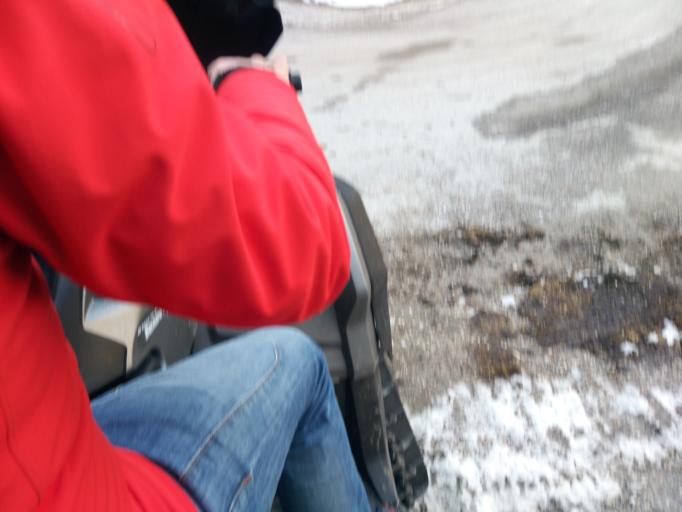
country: IT
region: Veneto
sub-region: Provincia di Belluno
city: Alleghe
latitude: 46.4191
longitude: 12.0057
